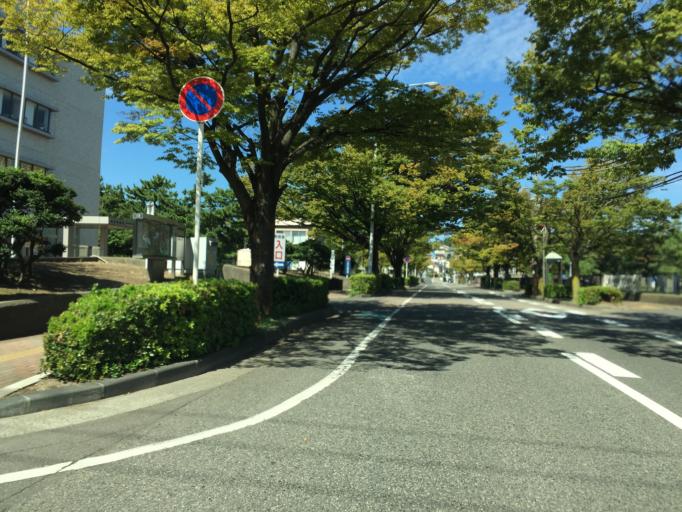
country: JP
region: Niigata
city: Niigata-shi
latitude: 37.9272
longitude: 139.0429
